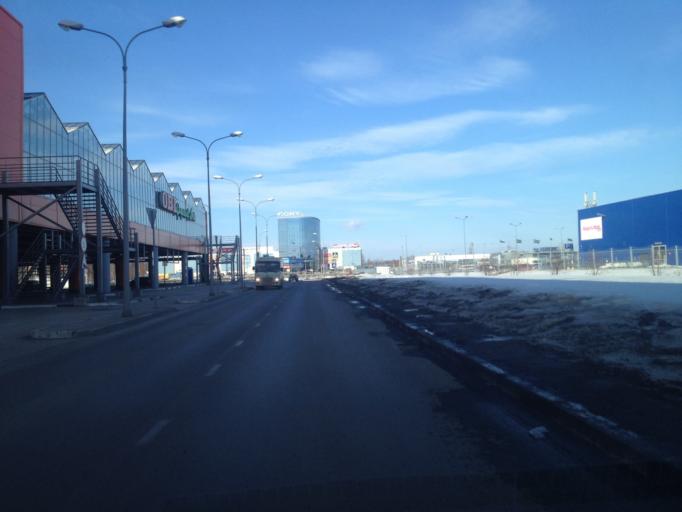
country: RU
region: Sverdlovsk
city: Shirokaya Rechka
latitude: 56.8238
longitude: 60.5094
